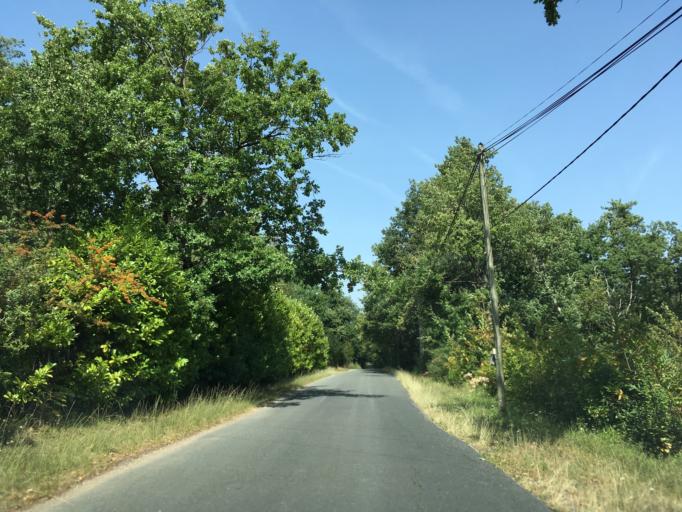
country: FR
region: Midi-Pyrenees
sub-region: Departement du Tarn
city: Lagarrigue
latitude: 43.5997
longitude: 2.3010
